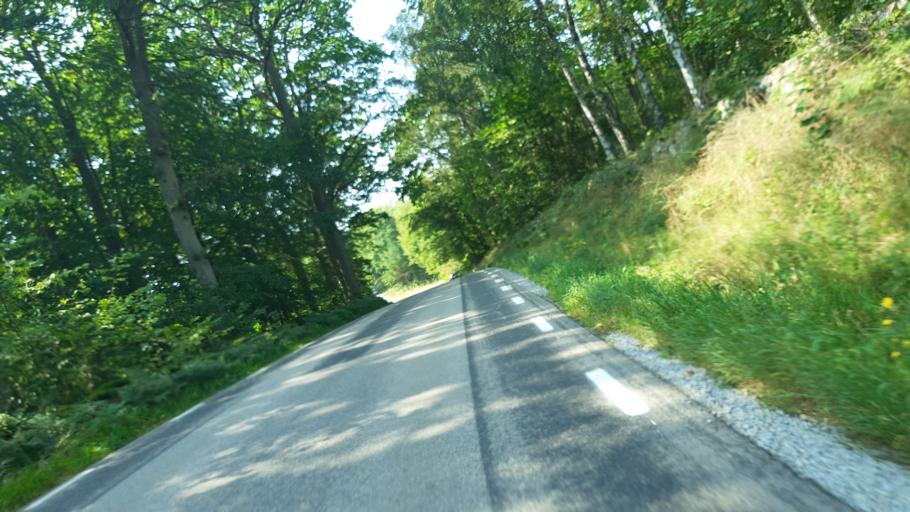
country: SE
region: Blekinge
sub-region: Ronneby Kommun
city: Ronneby
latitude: 56.1629
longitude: 15.2162
